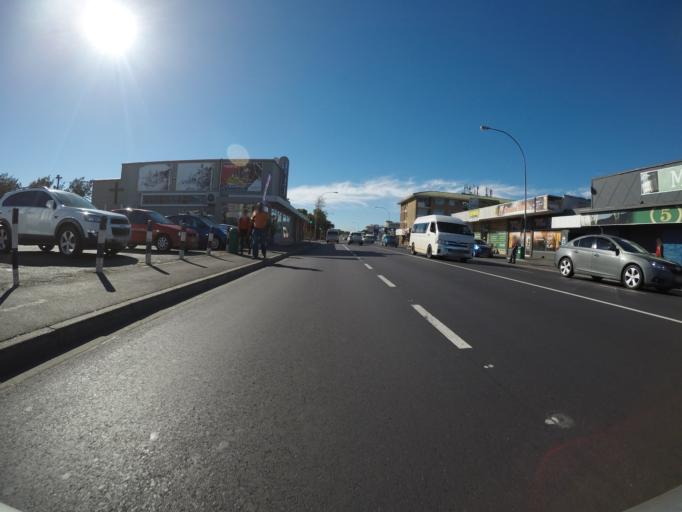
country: ZA
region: Western Cape
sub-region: City of Cape Town
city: Kraaifontein
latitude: -33.9220
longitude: 18.6764
